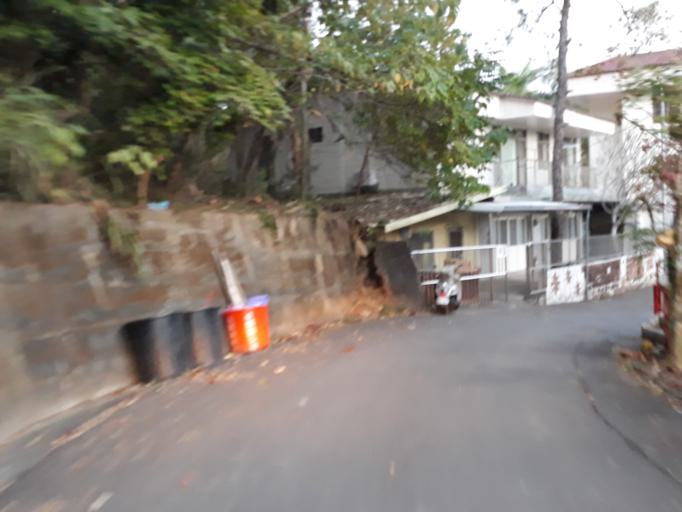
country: TW
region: Taiwan
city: Fengyuan
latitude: 24.3527
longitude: 120.8645
